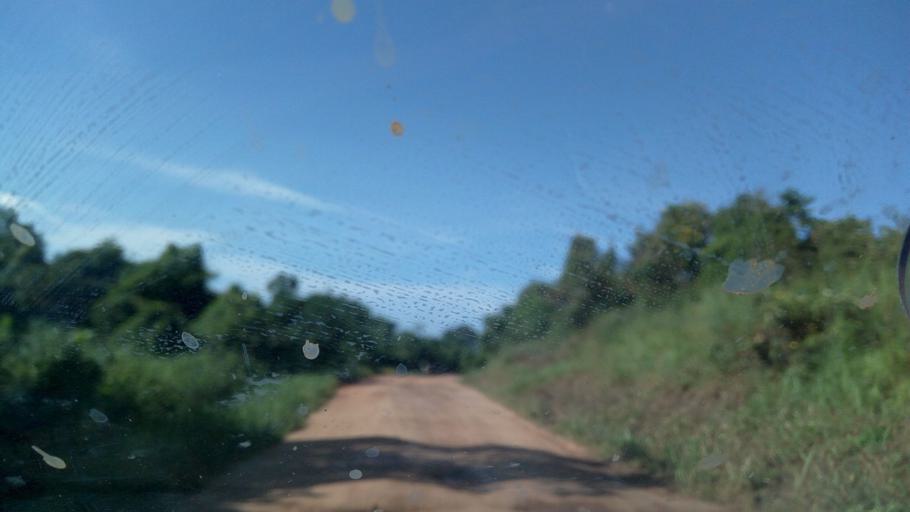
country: BI
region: Bururi
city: Rumonge
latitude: -4.3382
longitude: 28.9389
